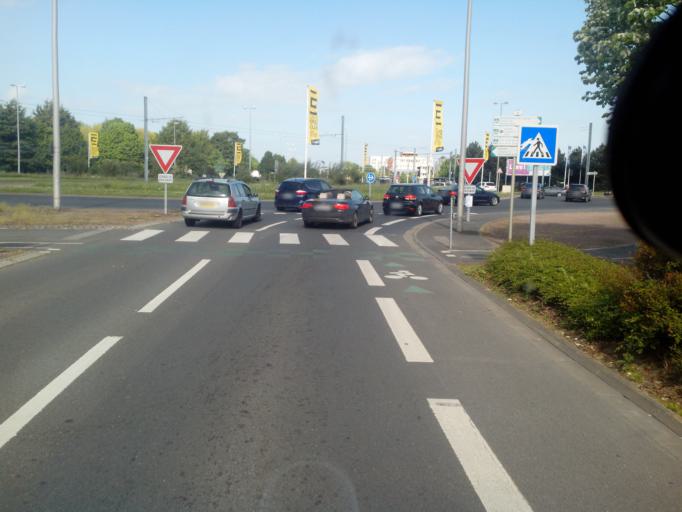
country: FR
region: Lower Normandy
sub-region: Departement du Calvados
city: Epron
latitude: 49.2105
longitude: -0.3640
